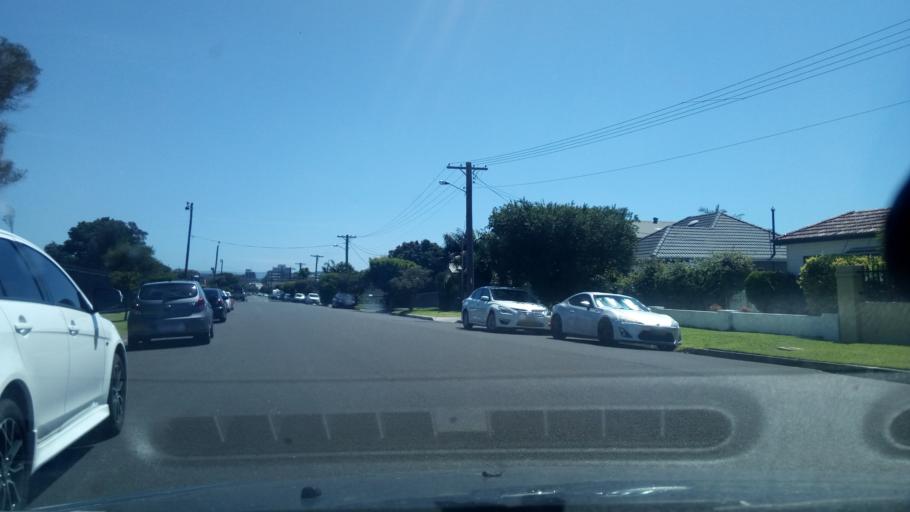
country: AU
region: New South Wales
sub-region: Wollongong
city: Wollongong
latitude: -34.4376
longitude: 150.8902
